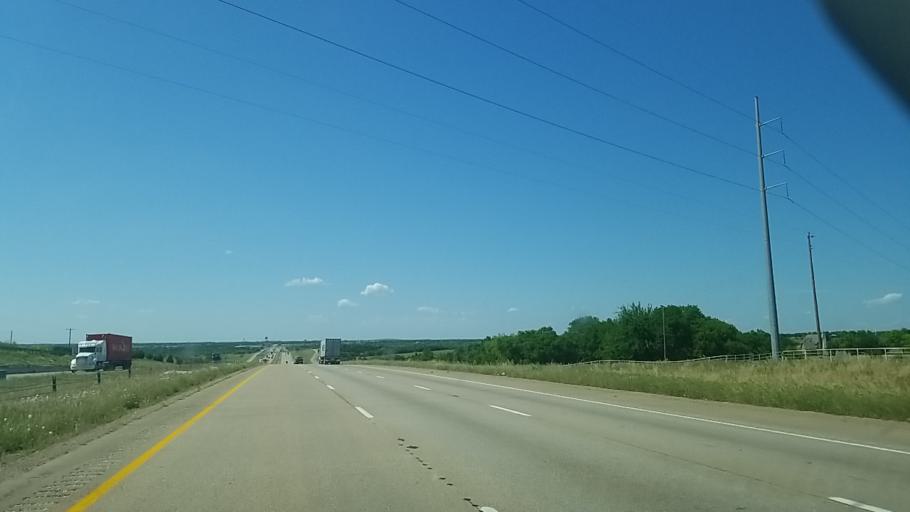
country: US
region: Texas
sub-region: Ellis County
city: Palmer
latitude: 32.3855
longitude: -96.6497
